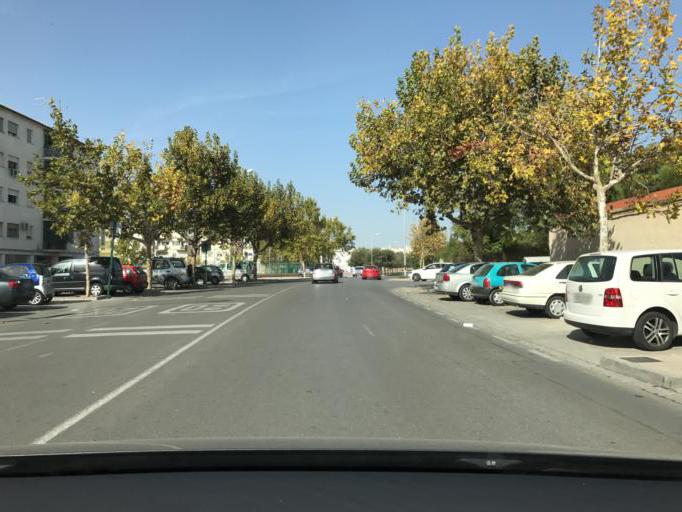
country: ES
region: Andalusia
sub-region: Provincia de Granada
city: Pulianas
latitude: 37.2066
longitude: -3.6041
